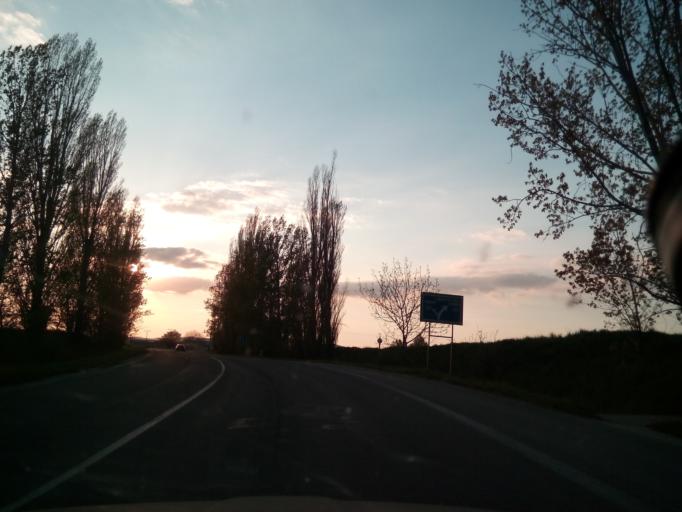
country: SK
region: Trnavsky
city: Vrbove
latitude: 48.5911
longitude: 17.7522
